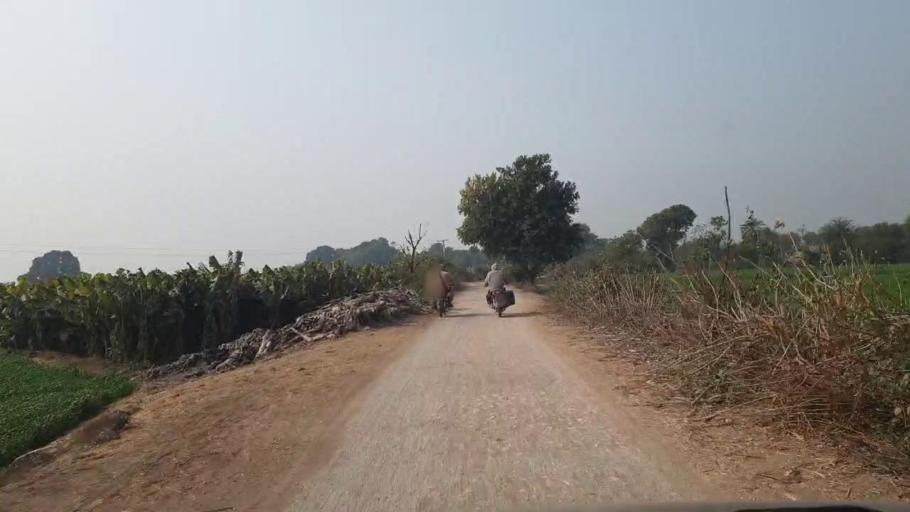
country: PK
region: Sindh
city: Hala
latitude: 25.8995
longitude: 68.3516
